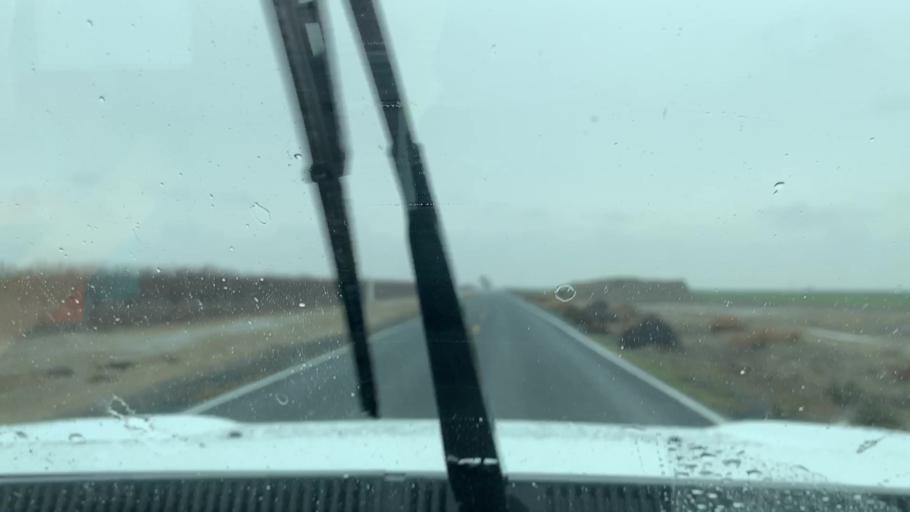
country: US
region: California
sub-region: Tulare County
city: Earlimart
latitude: 35.8917
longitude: -119.3680
